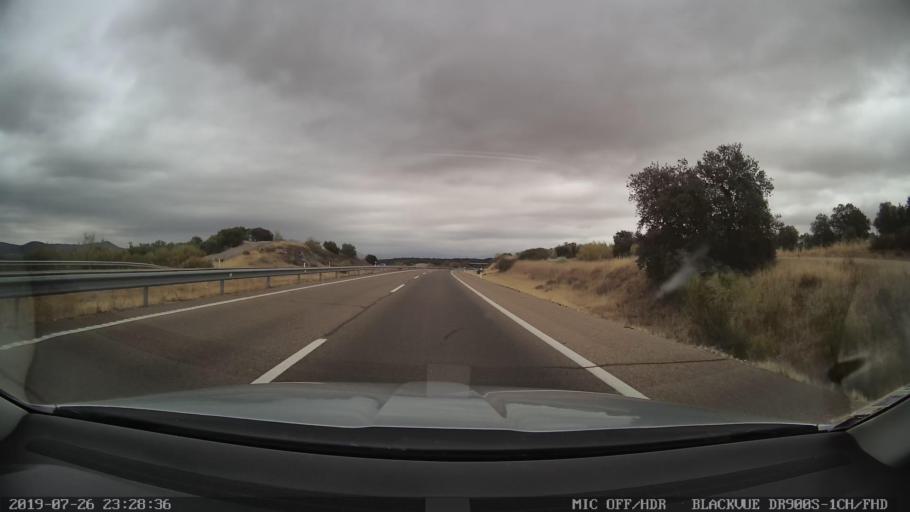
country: ES
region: Extremadura
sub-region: Provincia de Caceres
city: Villamesias
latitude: 39.2492
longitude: -5.8786
